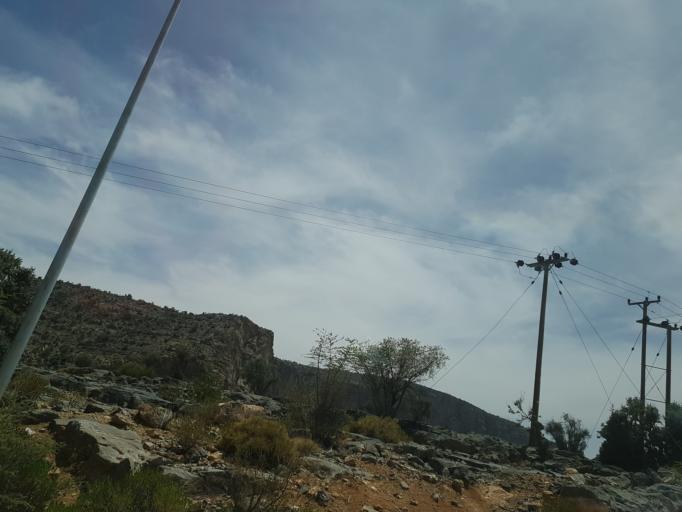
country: OM
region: Al Batinah
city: Bayt al `Awabi
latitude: 23.1354
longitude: 57.5595
